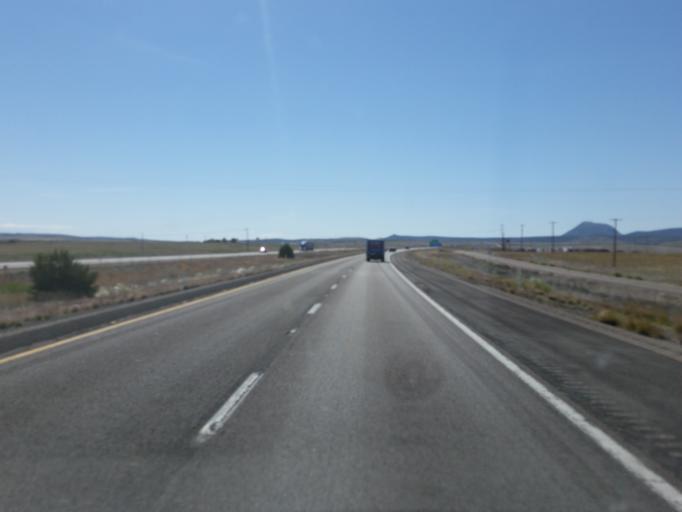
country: US
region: Arizona
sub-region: Yavapai County
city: Paulden
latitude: 35.3140
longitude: -112.8639
